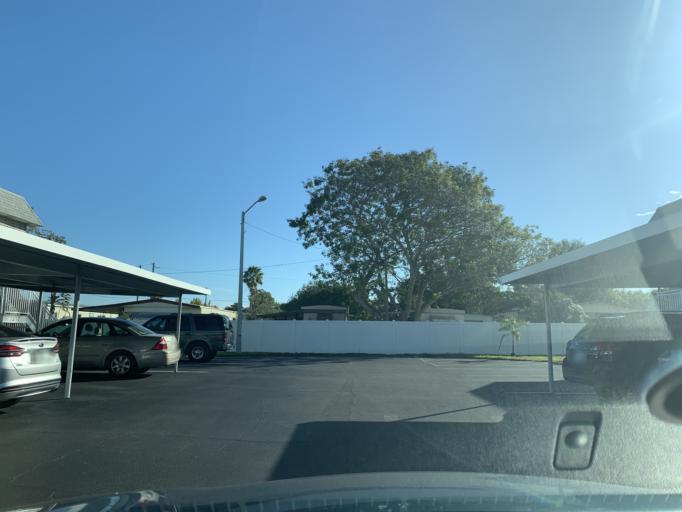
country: US
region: Florida
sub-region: Pinellas County
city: Bay Pines
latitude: 27.8205
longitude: -82.7500
